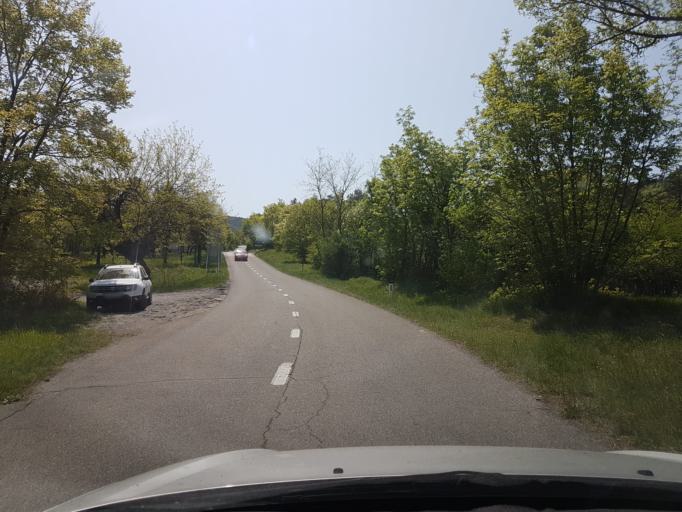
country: IT
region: Friuli Venezia Giulia
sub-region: Provincia di Trieste
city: Aurisina
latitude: 45.7820
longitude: 13.6996
